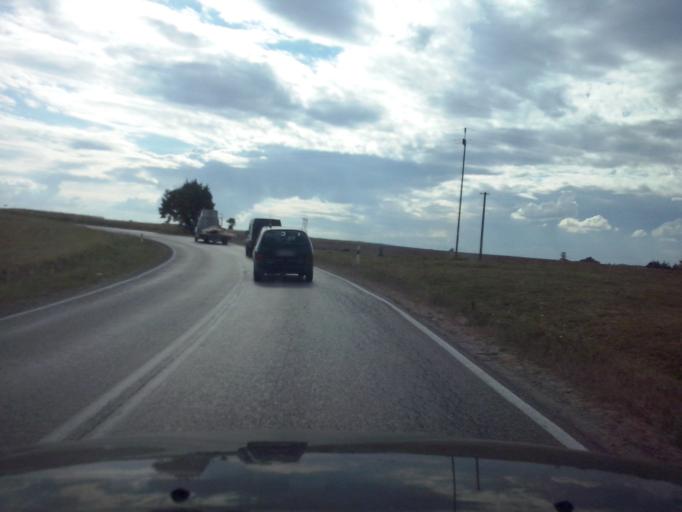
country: PL
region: Swietokrzyskie
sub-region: Powiat kielecki
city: Lagow
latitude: 50.7513
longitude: 21.0761
